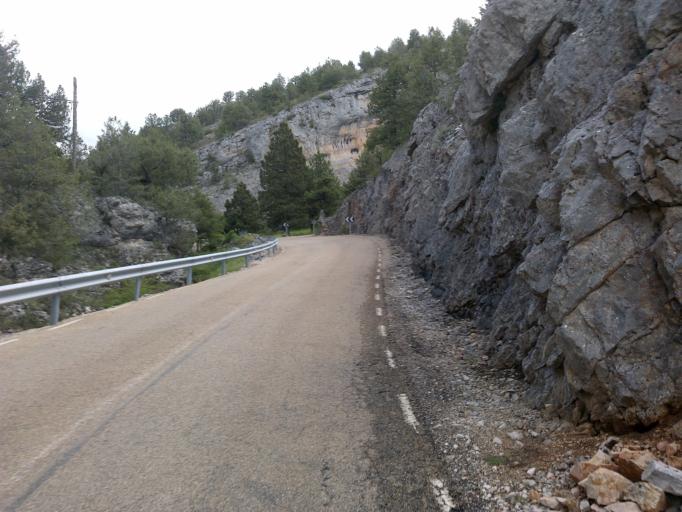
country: ES
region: Castille and Leon
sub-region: Provincia de Burgos
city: Carazo
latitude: 41.9564
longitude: -3.3786
